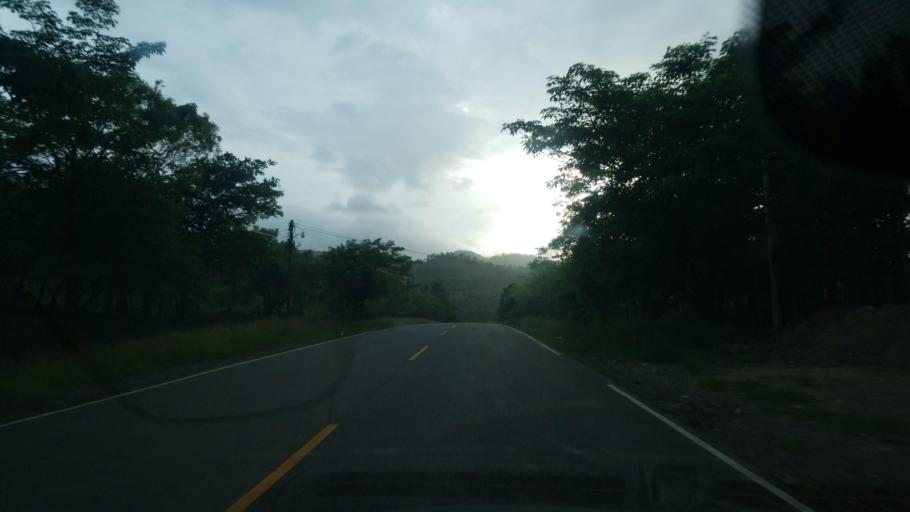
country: HN
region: Ocotepeque
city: Sinuapa
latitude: 14.5175
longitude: -89.2391
